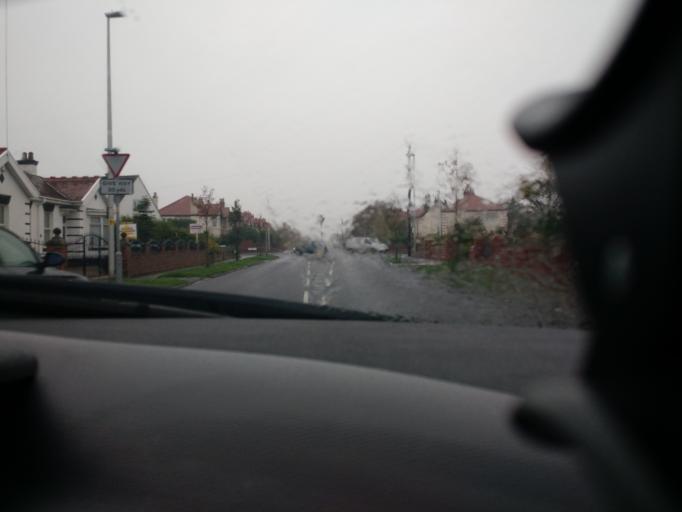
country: GB
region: England
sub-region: Lancashire
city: Cleveleys
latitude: 53.8732
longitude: -3.0322
